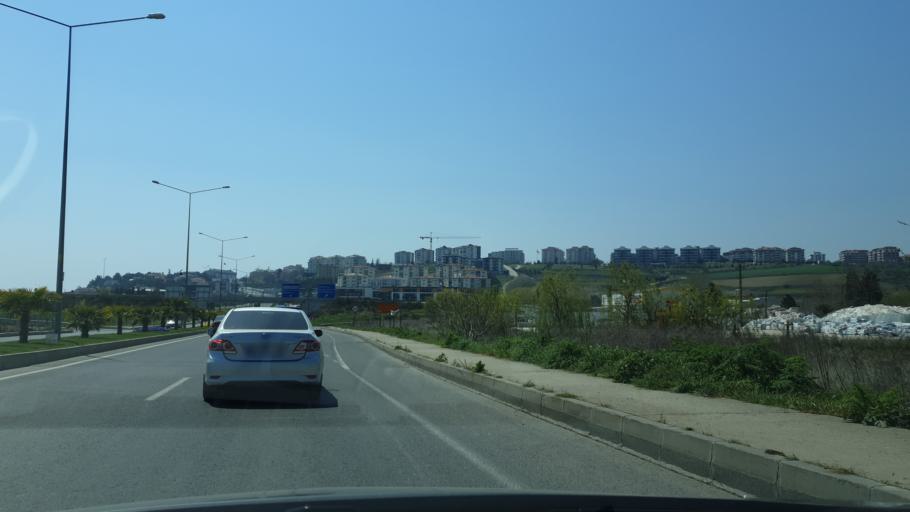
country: TR
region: Tekirdag
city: Tekirdag
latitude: 40.9919
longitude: 27.5764
